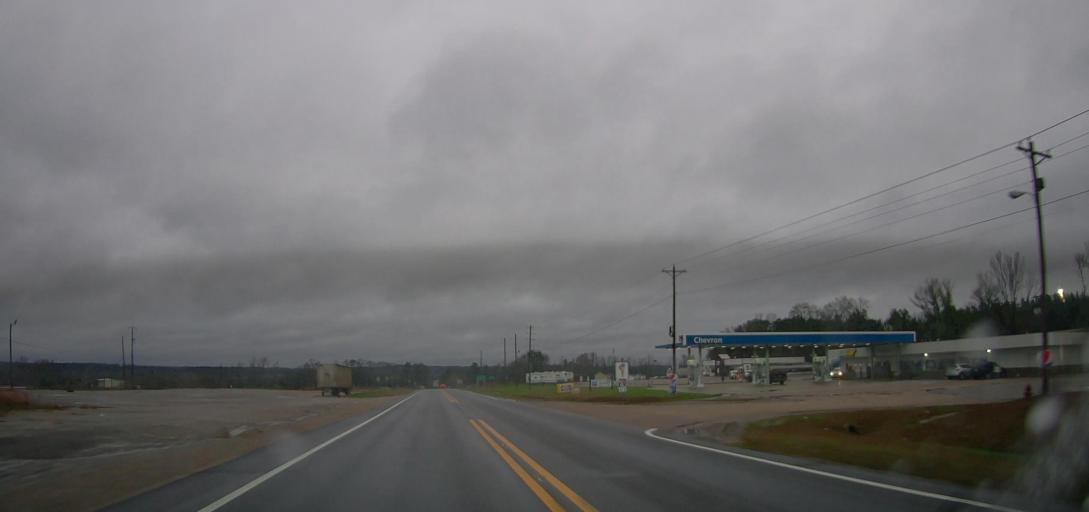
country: US
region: Alabama
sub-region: Chilton County
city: Thorsby
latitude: 32.7710
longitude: -86.8810
